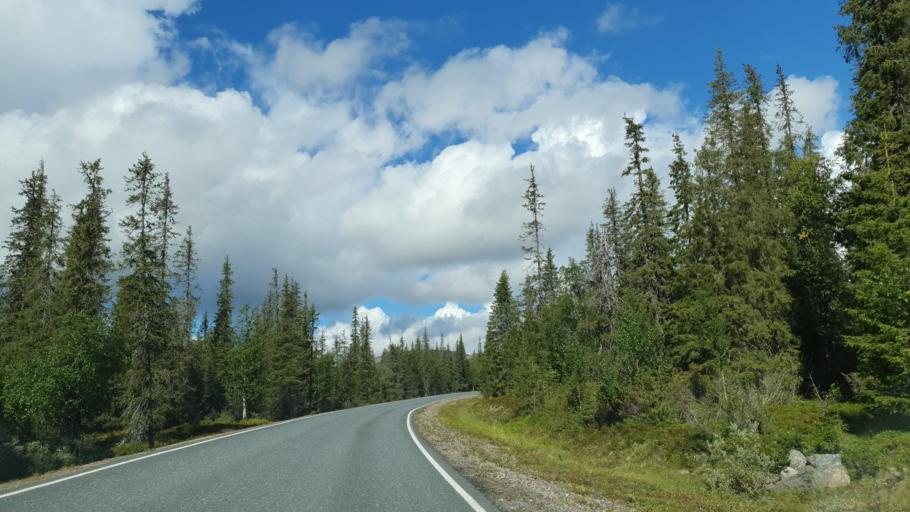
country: FI
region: Lapland
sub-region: Tunturi-Lappi
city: Muonio
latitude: 68.0362
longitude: 24.0661
